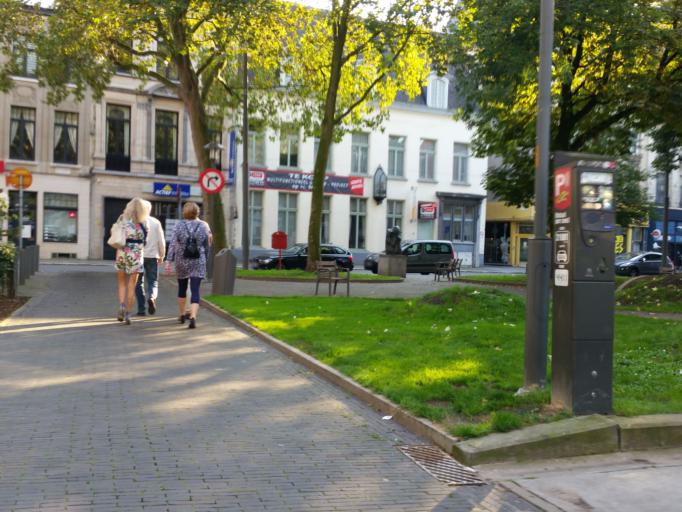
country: BE
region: Flanders
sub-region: Provincie Antwerpen
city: Antwerpen
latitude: 51.2207
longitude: 4.4121
